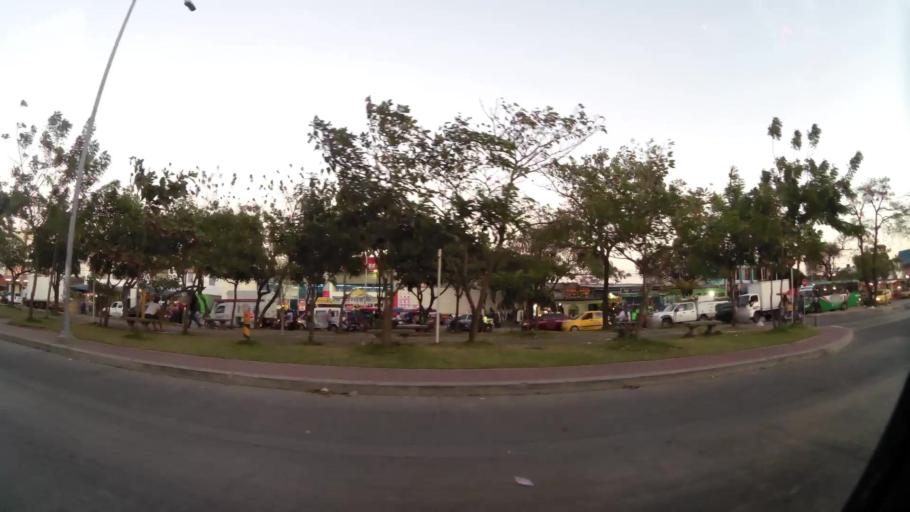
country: CO
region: Atlantico
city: Barranquilla
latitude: 10.9419
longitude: -74.7780
